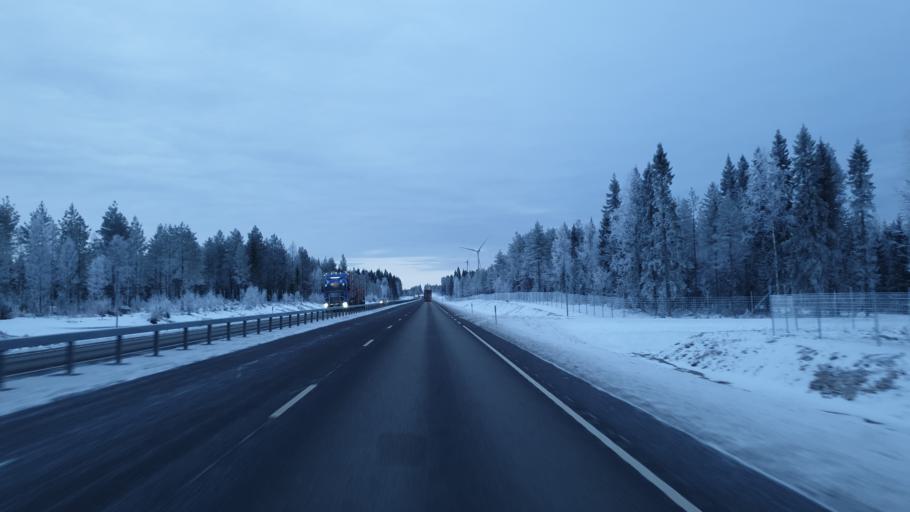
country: FI
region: Lapland
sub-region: Kemi-Tornio
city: Simo
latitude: 65.6471
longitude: 25.0985
